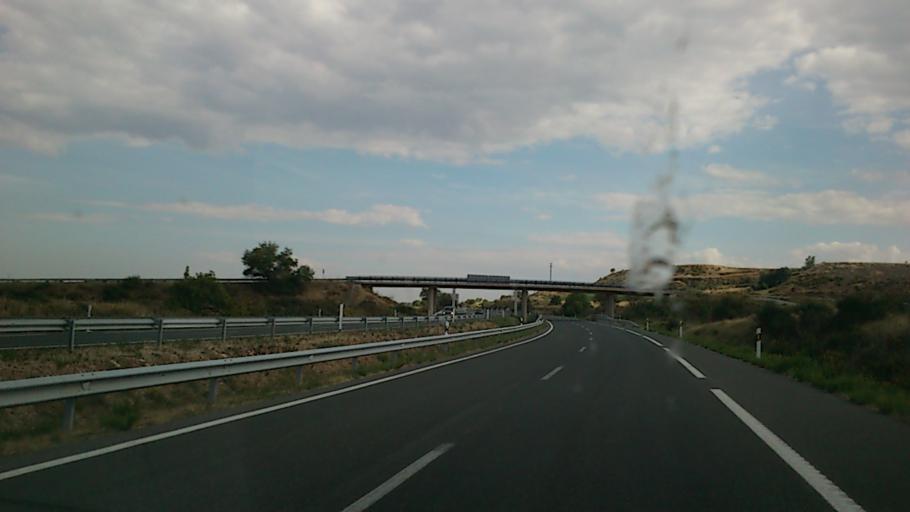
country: ES
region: La Rioja
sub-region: Provincia de La Rioja
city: Haro
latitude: 42.5539
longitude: -2.8652
